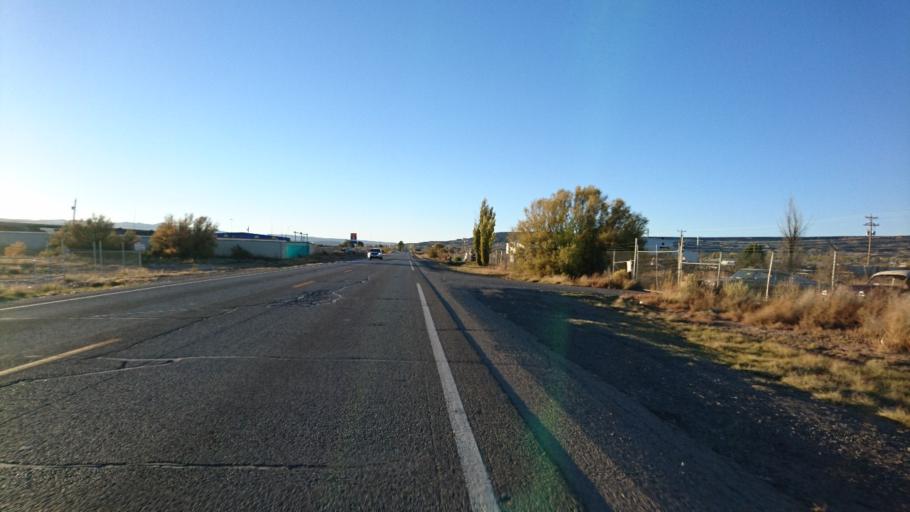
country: US
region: New Mexico
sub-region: Cibola County
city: Grants
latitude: 35.1371
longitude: -107.8233
